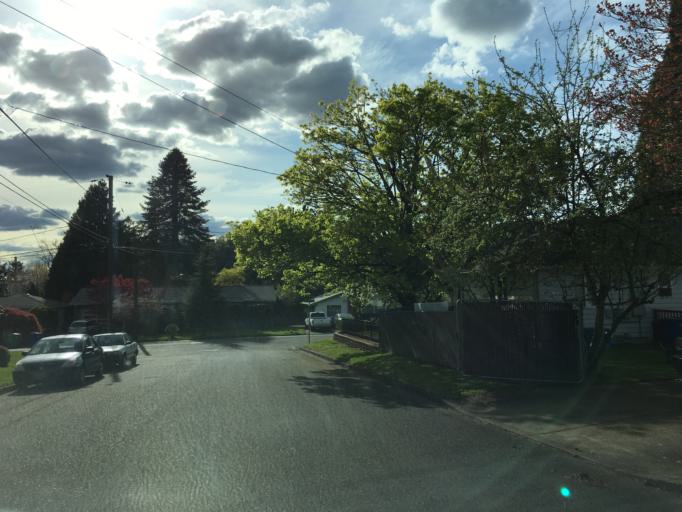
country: US
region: Oregon
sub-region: Multnomah County
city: Lents
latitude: 45.5413
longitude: -122.5543
